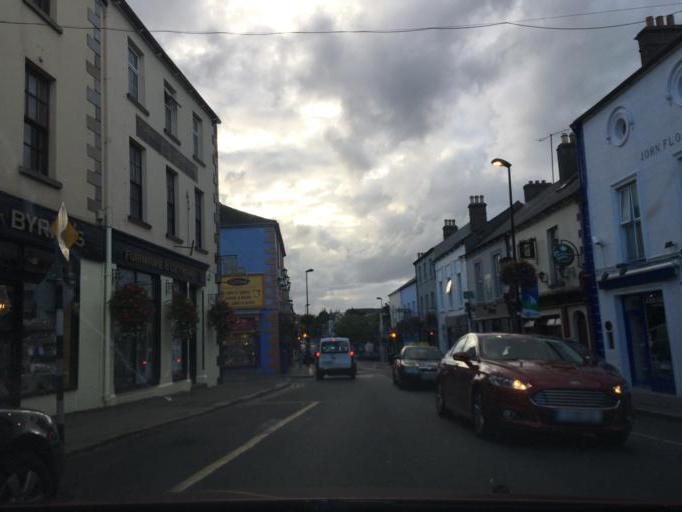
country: IE
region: Leinster
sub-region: Wicklow
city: Wicklow
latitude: 52.9804
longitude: -6.0416
